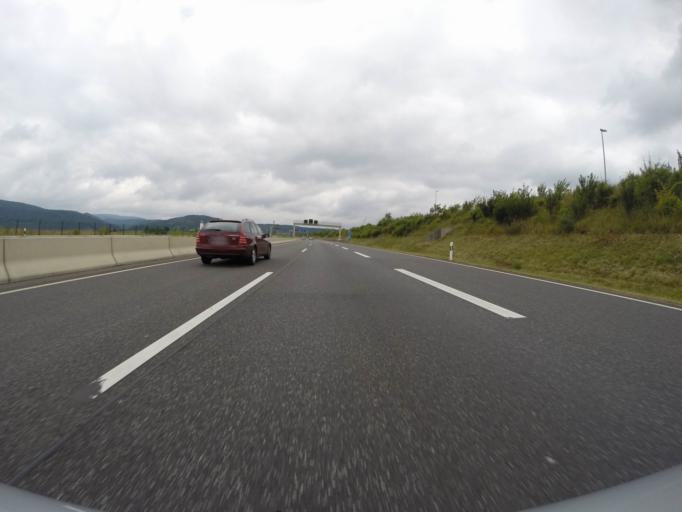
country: DE
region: Thuringia
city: Geraberg
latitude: 50.7257
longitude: 10.8440
